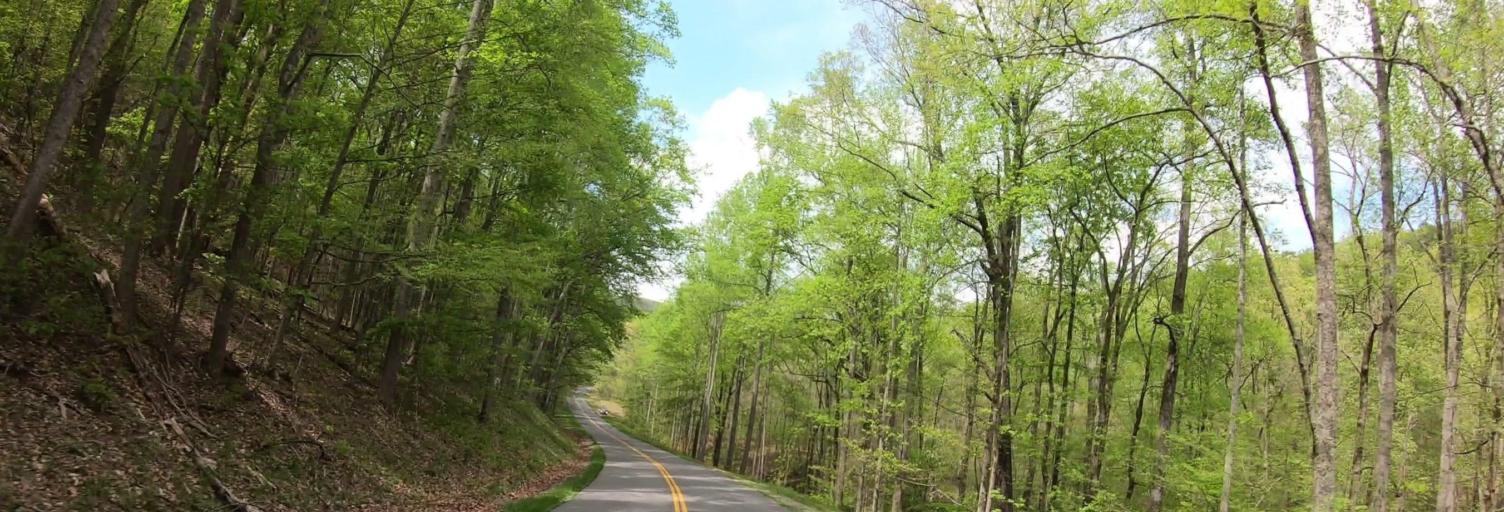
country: US
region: Virginia
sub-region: Botetourt County
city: Laymantown
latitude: 37.3896
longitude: -79.8377
